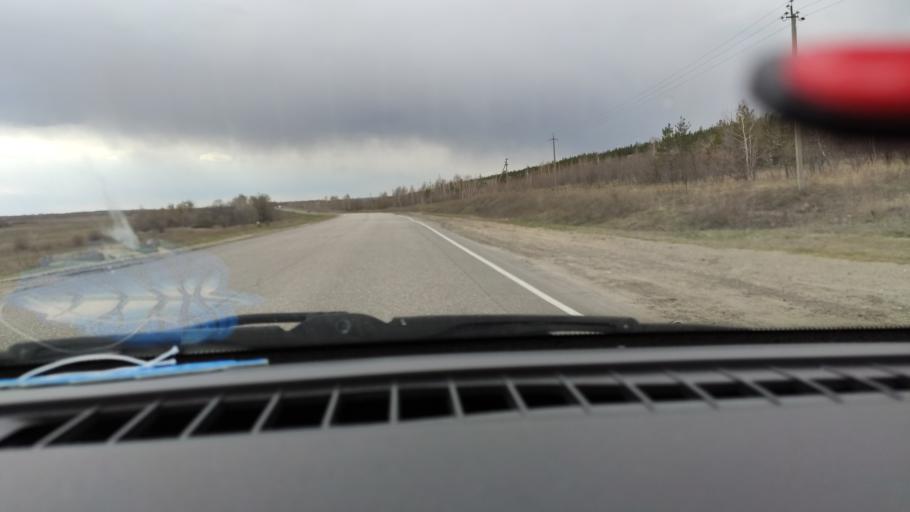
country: RU
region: Saratov
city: Sinodskoye
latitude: 52.0622
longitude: 46.7648
